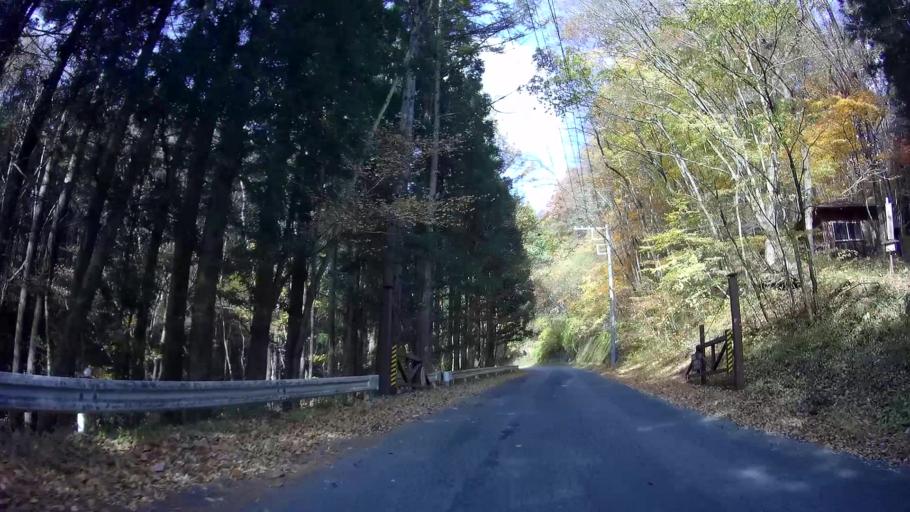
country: JP
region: Gunma
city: Nakanojomachi
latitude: 36.5130
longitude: 138.6722
